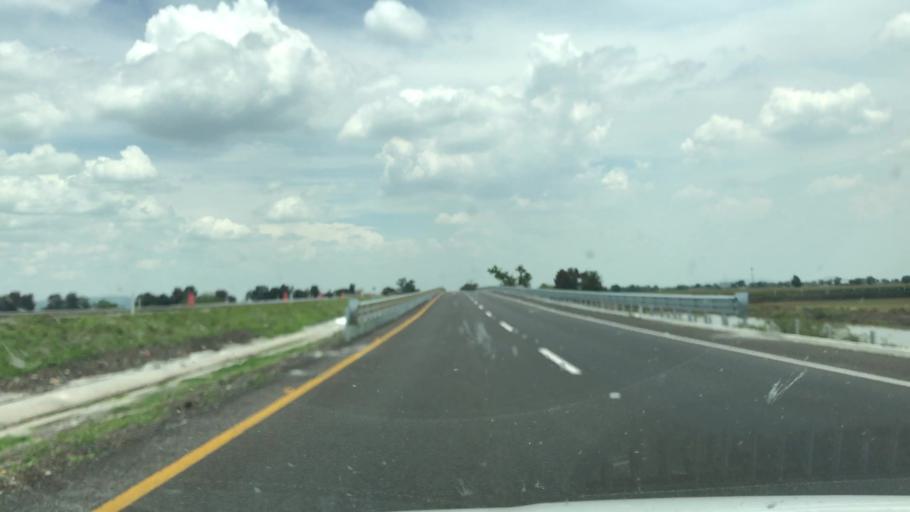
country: MX
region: Guanajuato
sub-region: Salamanca
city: San Vicente de Flores
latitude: 20.6375
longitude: -101.2609
